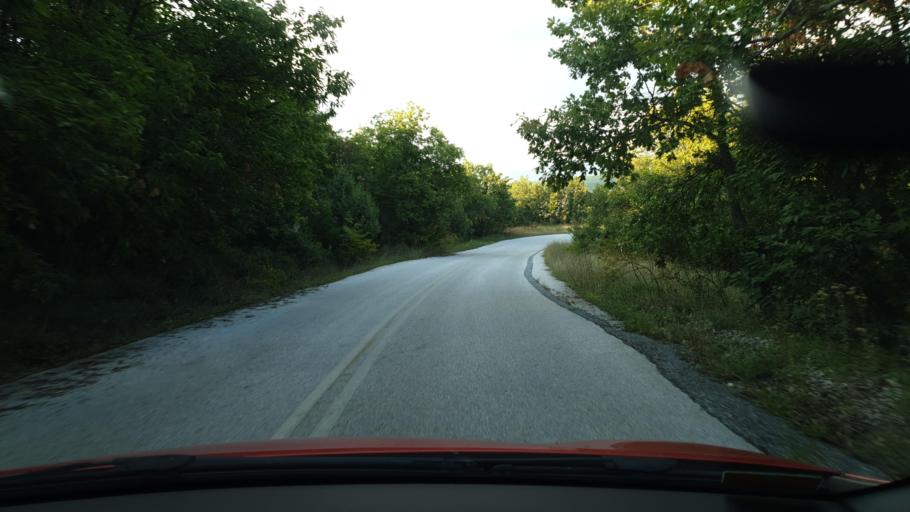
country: GR
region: Central Macedonia
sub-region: Nomos Chalkidikis
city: Galatista
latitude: 40.5134
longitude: 23.2683
